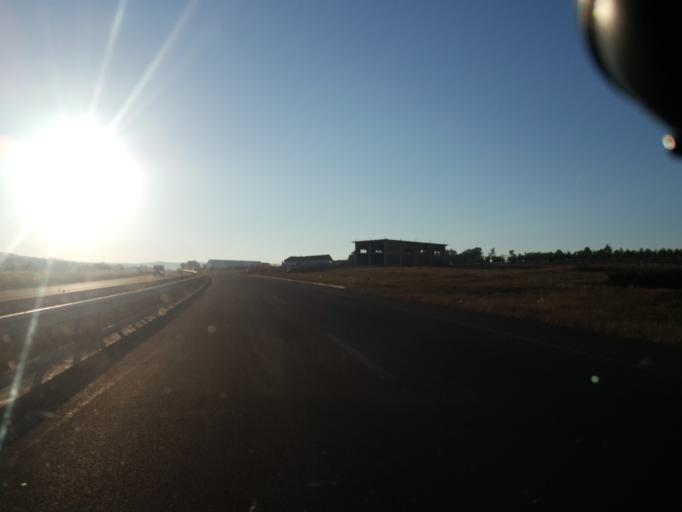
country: XK
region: Prizren
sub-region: Komuna e Malisheves
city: Llazice
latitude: 42.5694
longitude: 20.7372
